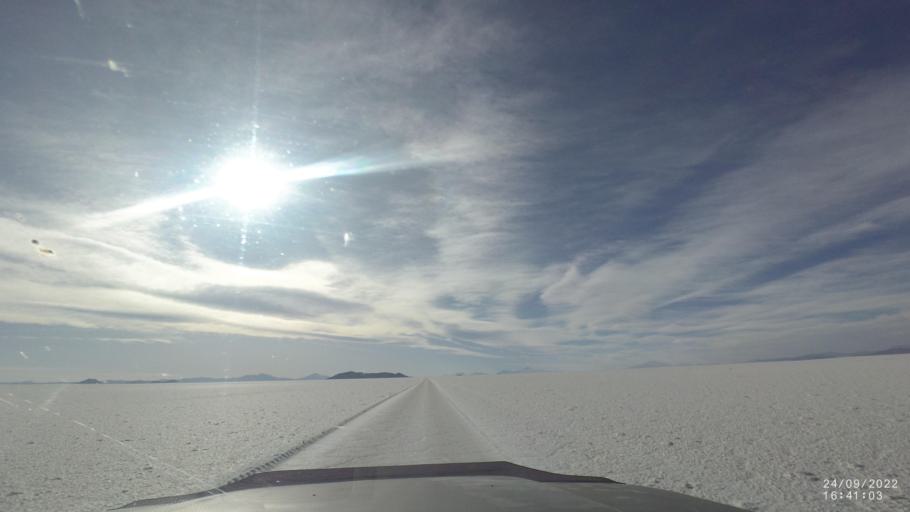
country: BO
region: Potosi
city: Colchani
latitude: -20.1887
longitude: -67.7096
